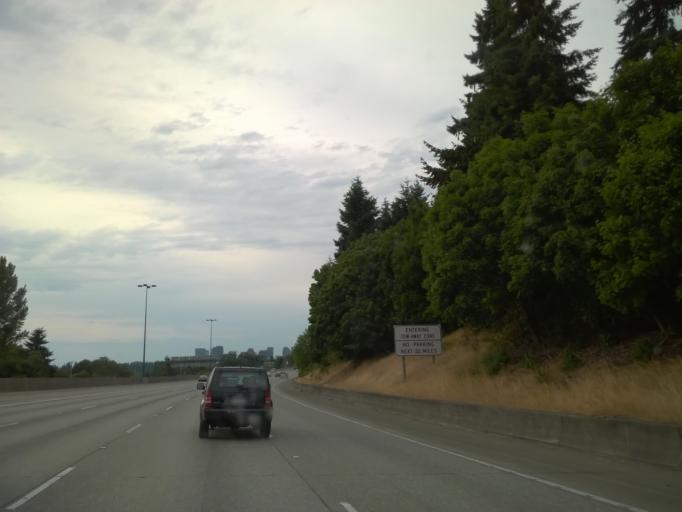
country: US
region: Washington
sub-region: King County
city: Newport
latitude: 47.5871
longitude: -122.1792
